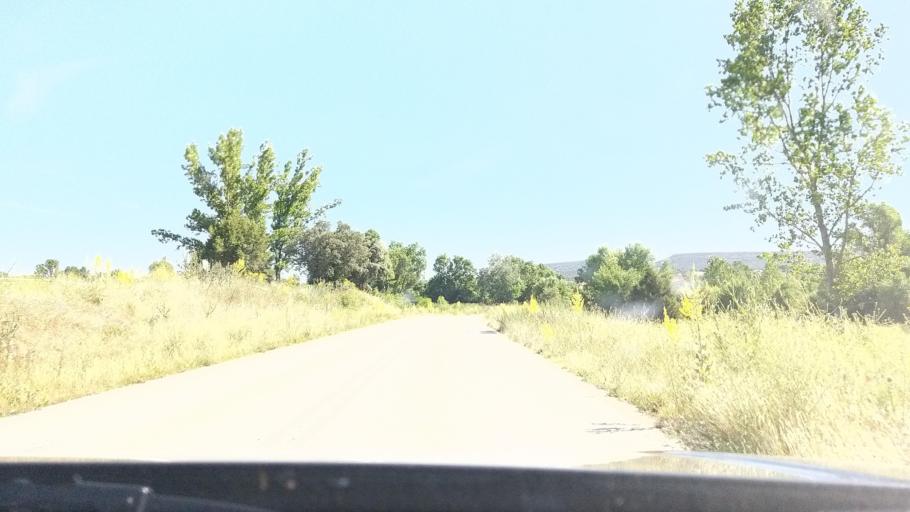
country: ES
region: Castille and Leon
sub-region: Provincia de Segovia
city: Pedraza
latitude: 41.1394
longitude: -3.8316
